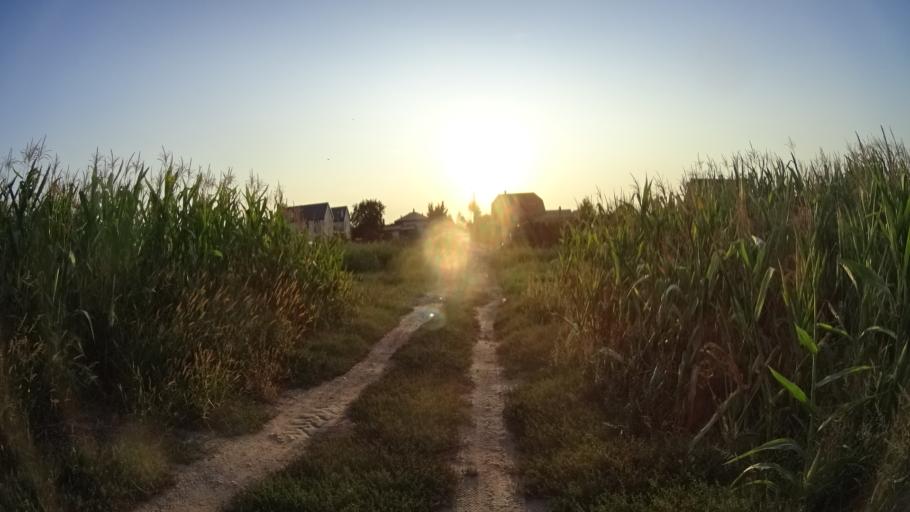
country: PL
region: Masovian Voivodeship
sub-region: Powiat warszawski zachodni
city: Ozarow Mazowiecki
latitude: 52.2408
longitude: 20.7683
